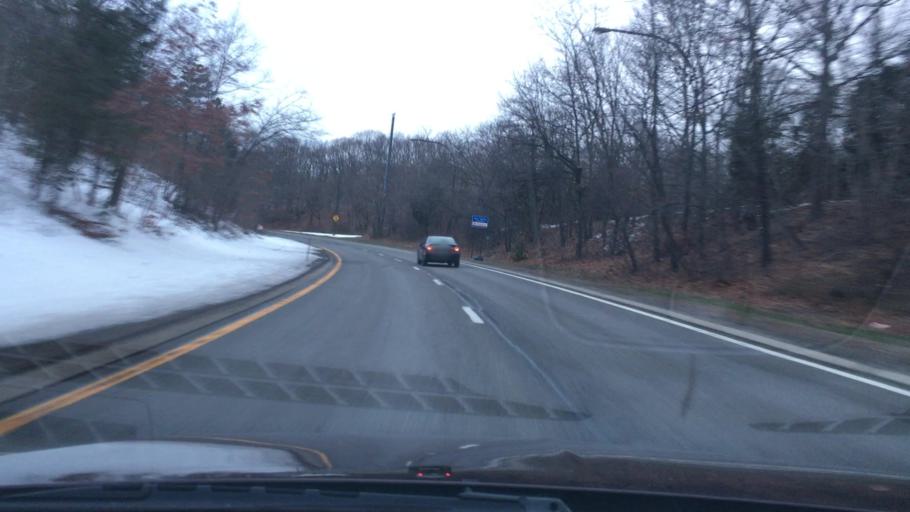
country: US
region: New York
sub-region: Suffolk County
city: Commack
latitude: 40.8307
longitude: -73.2544
